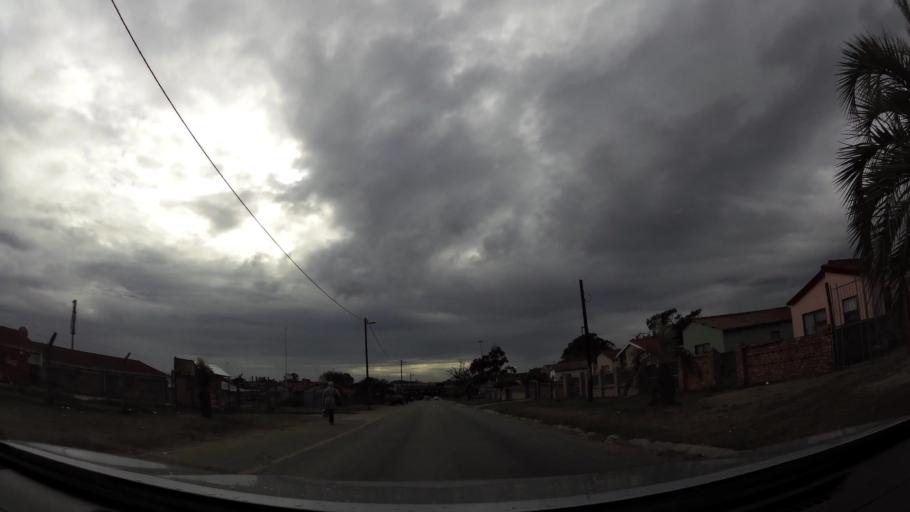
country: ZA
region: Eastern Cape
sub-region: Nelson Mandela Bay Metropolitan Municipality
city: Port Elizabeth
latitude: -33.9903
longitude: 25.5877
